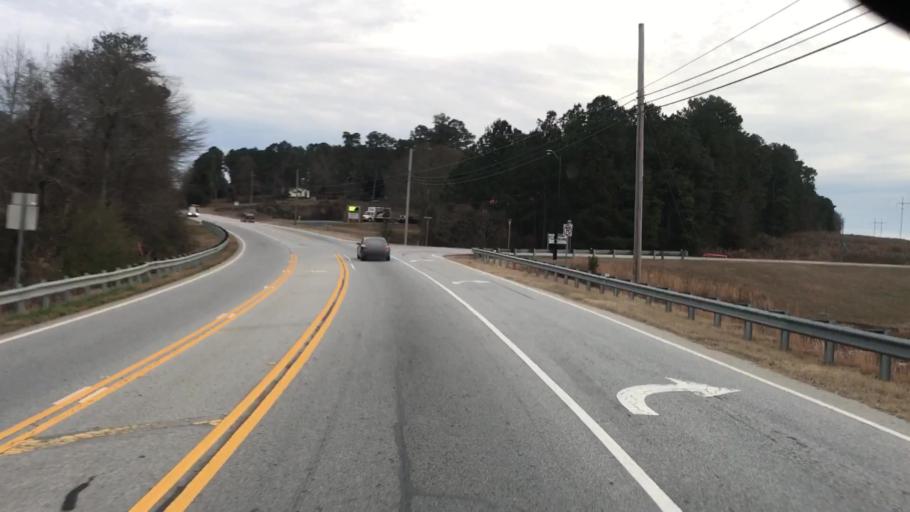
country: US
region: Georgia
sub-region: Barrow County
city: Winder
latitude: 34.0058
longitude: -83.7551
